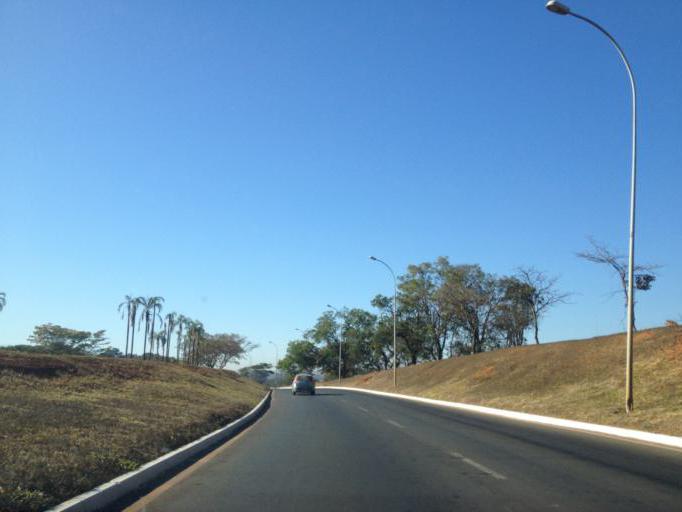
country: BR
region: Federal District
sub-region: Brasilia
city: Brasilia
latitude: -15.8366
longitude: -47.9267
